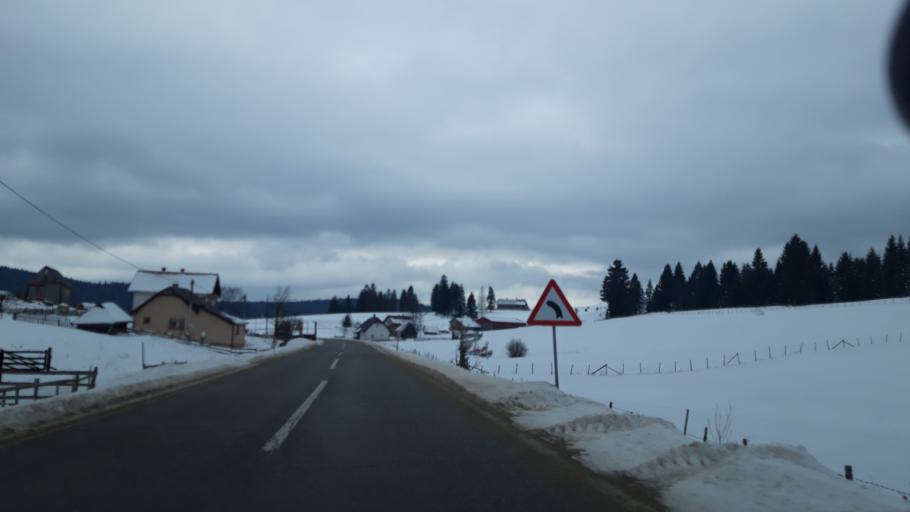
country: BA
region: Republika Srpska
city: Han Pijesak
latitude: 44.1120
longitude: 18.9686
